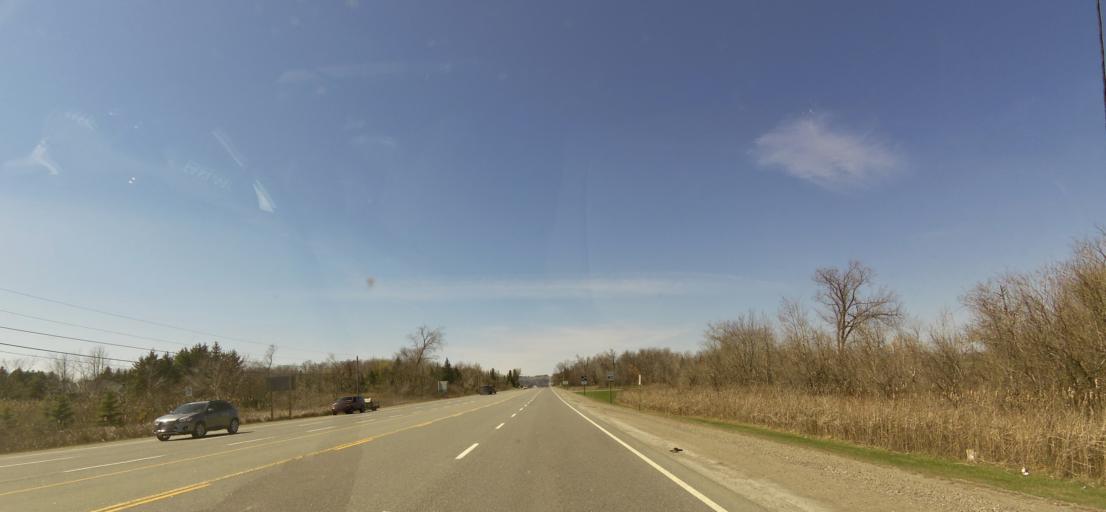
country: CA
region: Ontario
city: Brampton
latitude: 43.8014
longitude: -79.9162
